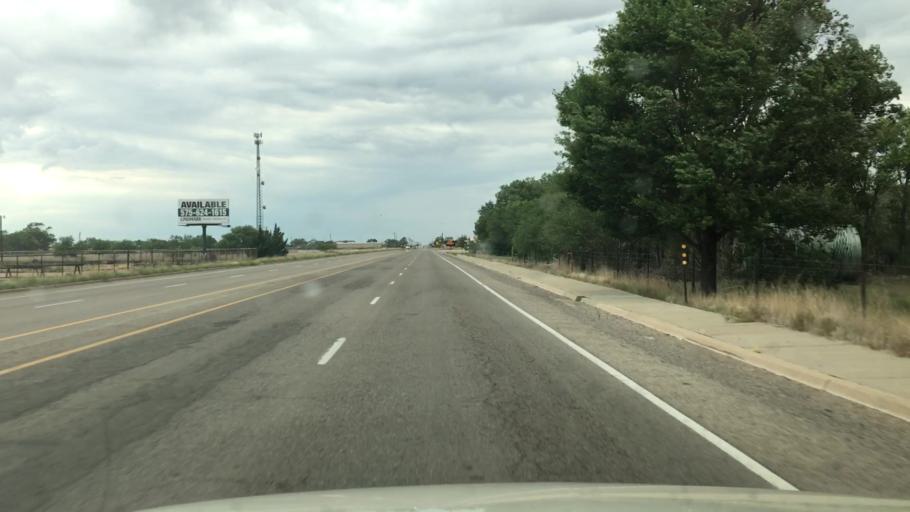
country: US
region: New Mexico
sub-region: Lea County
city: Lovington
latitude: 33.2570
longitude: -103.3281
